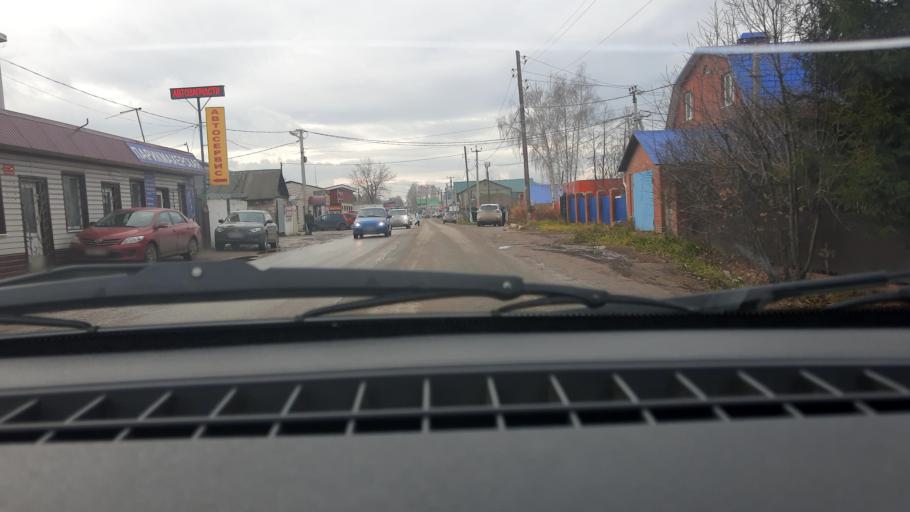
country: RU
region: Bashkortostan
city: Iglino
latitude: 54.8278
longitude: 56.4088
